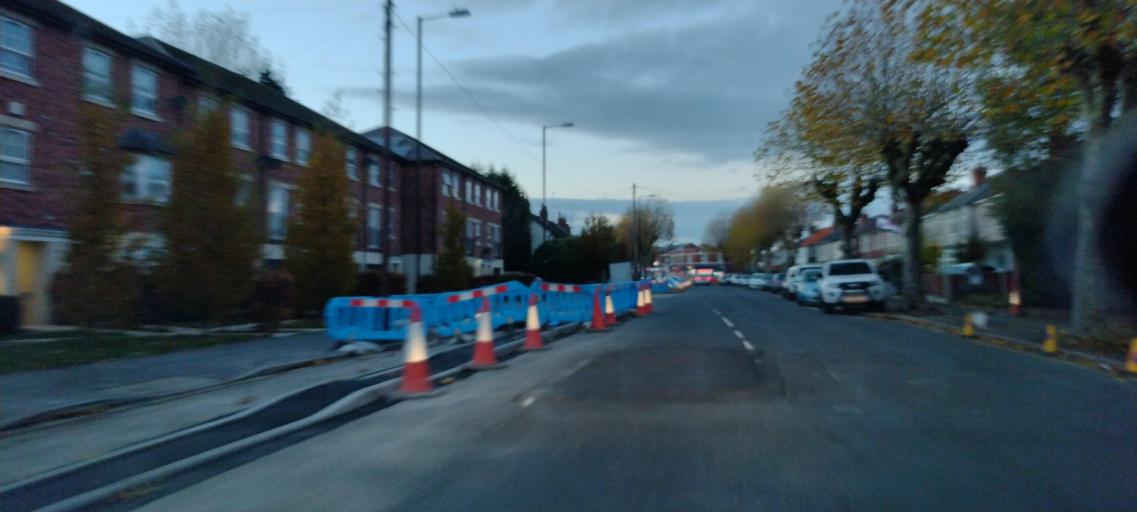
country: GB
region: England
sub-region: Coventry
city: Coventry
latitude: 52.4151
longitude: -1.5242
